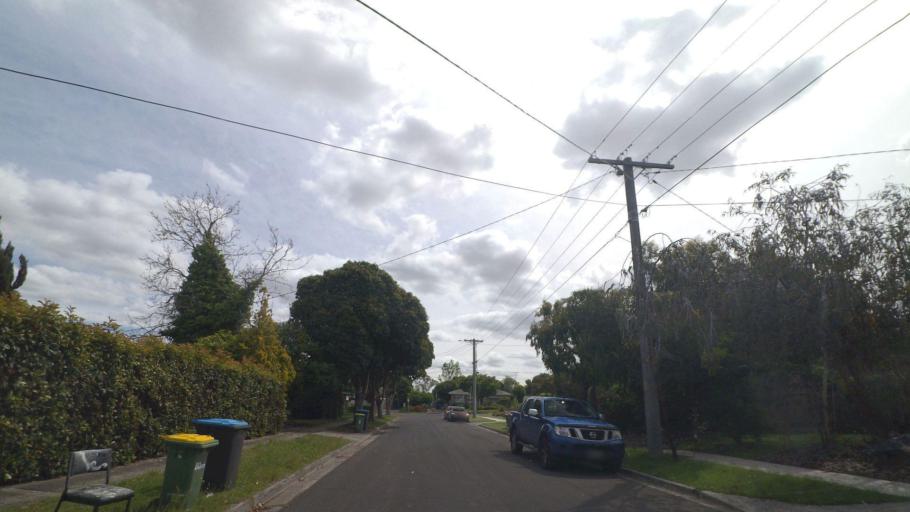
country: AU
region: Victoria
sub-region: Knox
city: Scoresby
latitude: -37.8977
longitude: 145.2351
